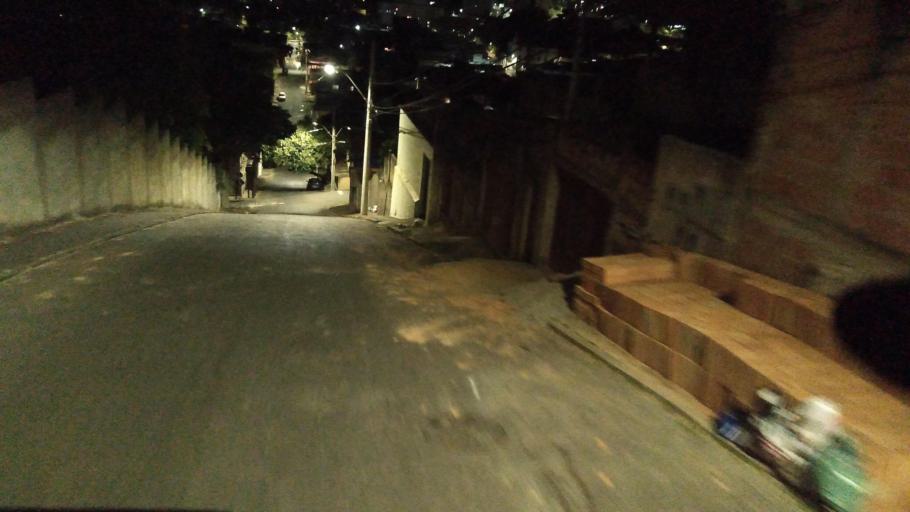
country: BR
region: Minas Gerais
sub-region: Belo Horizonte
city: Belo Horizonte
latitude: -19.8888
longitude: -43.9612
